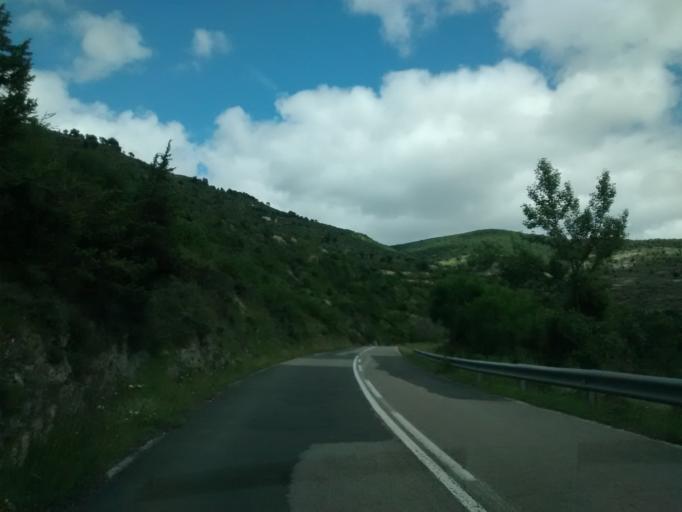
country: ES
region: La Rioja
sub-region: Provincia de La Rioja
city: Terroba
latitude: 42.2502
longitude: -2.4541
